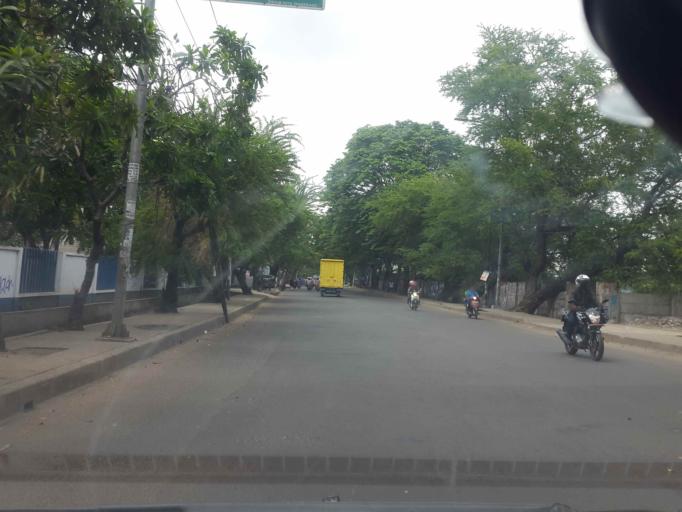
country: ID
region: Banten
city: Tangerang
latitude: -6.1707
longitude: 106.6136
